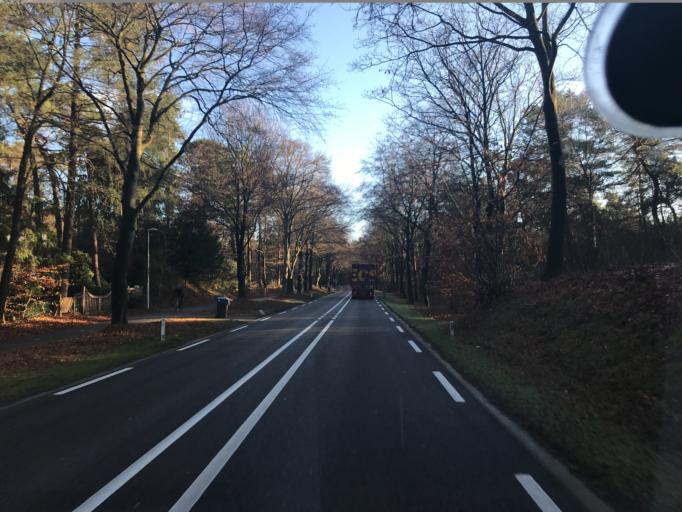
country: NL
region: Gelderland
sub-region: Gemeente Ermelo
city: Ermelo
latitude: 52.3197
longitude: 5.6594
